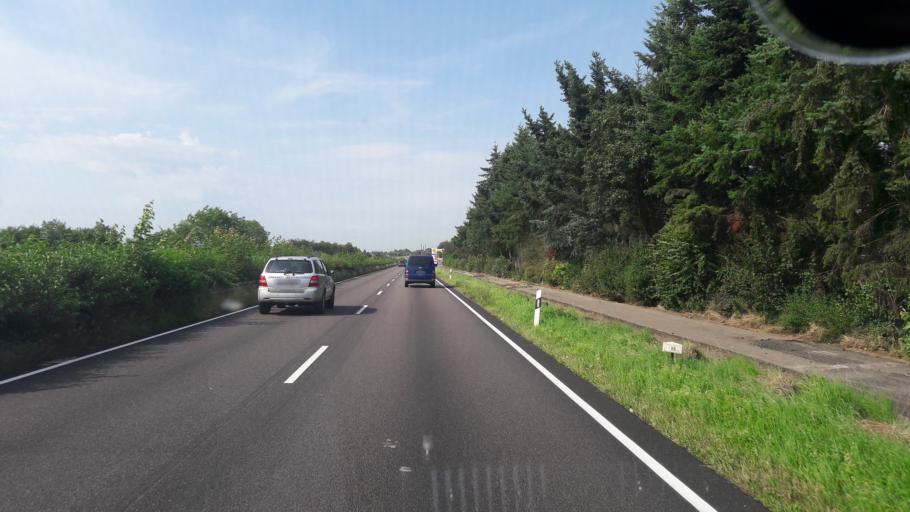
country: DE
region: Baden-Wuerttemberg
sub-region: Karlsruhe Region
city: Rheinstetten
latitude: 48.9569
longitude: 8.2962
